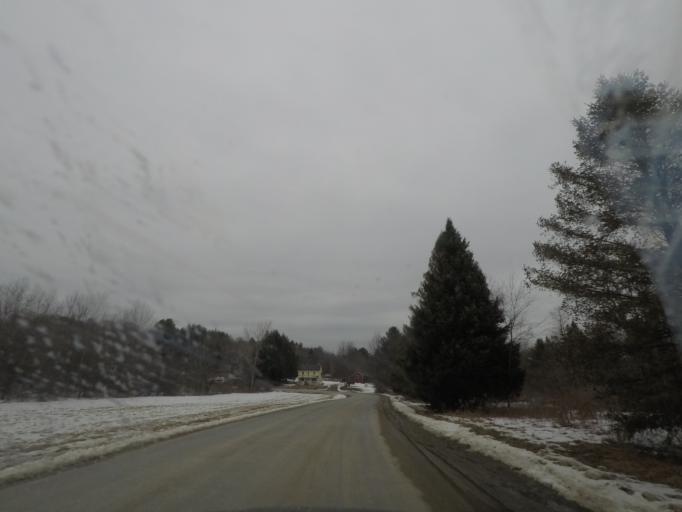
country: US
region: Massachusetts
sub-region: Berkshire County
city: Richmond
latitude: 42.5379
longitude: -73.4038
